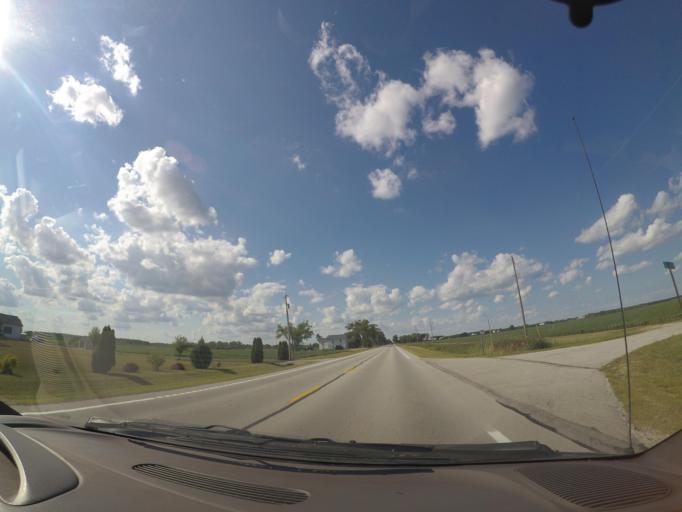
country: US
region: Ohio
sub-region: Sandusky County
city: Woodville
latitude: 41.4562
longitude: -83.4151
